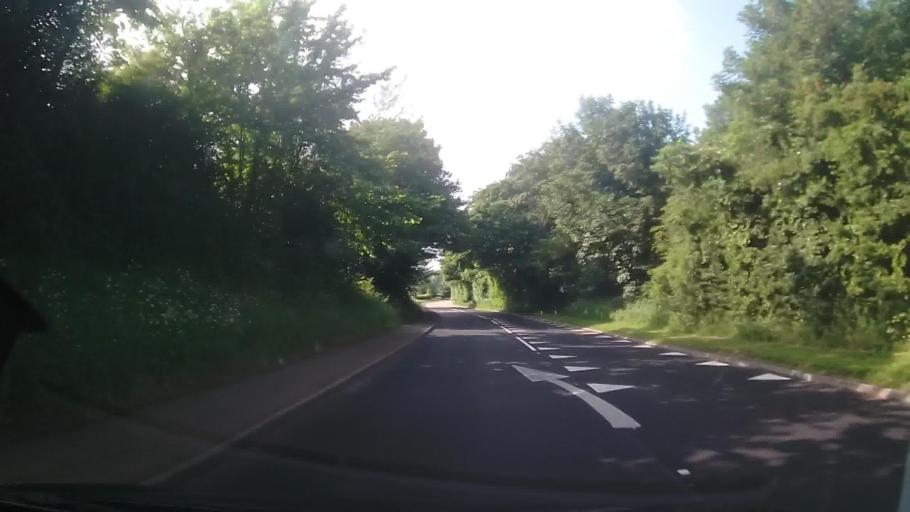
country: GB
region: England
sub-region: Shropshire
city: Longnor
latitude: 52.6248
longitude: -2.7768
